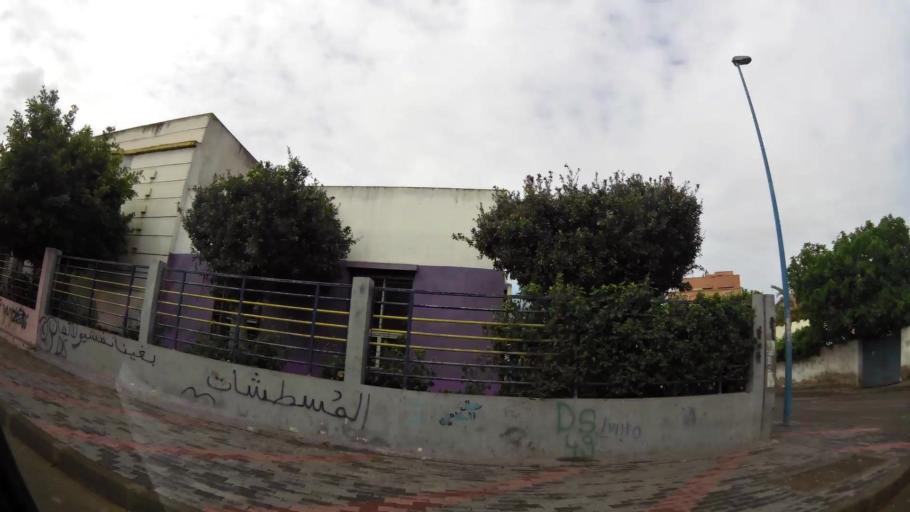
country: MA
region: Grand Casablanca
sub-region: Casablanca
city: Casablanca
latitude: 33.5715
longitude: -7.5918
